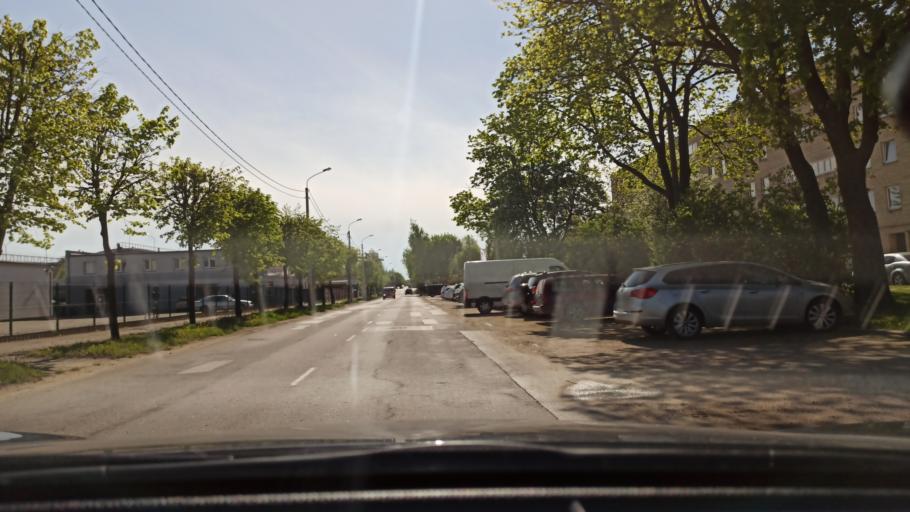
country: LT
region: Siauliu apskritis
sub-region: Siauliai
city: Siauliai
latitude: 55.9500
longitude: 23.3079
